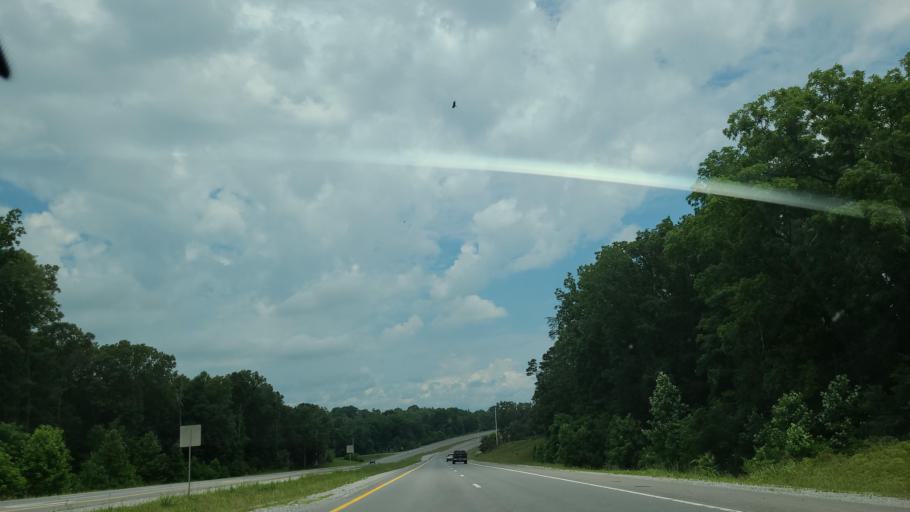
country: US
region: Tennessee
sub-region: Jefferson County
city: White Pine
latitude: 36.1563
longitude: -83.3438
